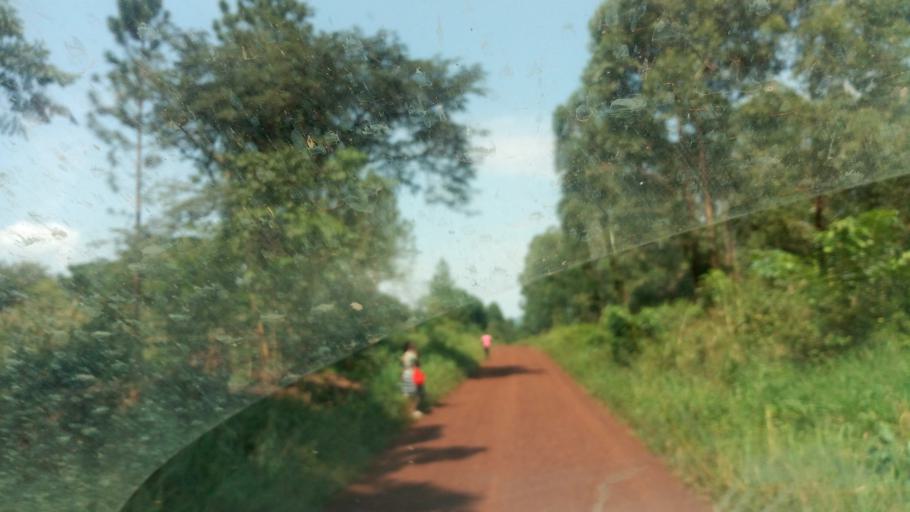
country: UG
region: Western Region
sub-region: Masindi District
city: Masindi
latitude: 1.6670
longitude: 31.8190
